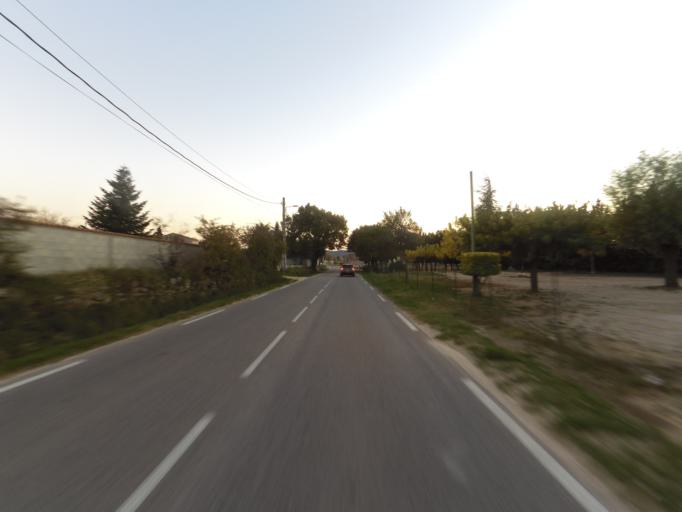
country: FR
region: Provence-Alpes-Cote d'Azur
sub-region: Departement du Vaucluse
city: Bedoin
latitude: 44.1141
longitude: 5.1774
